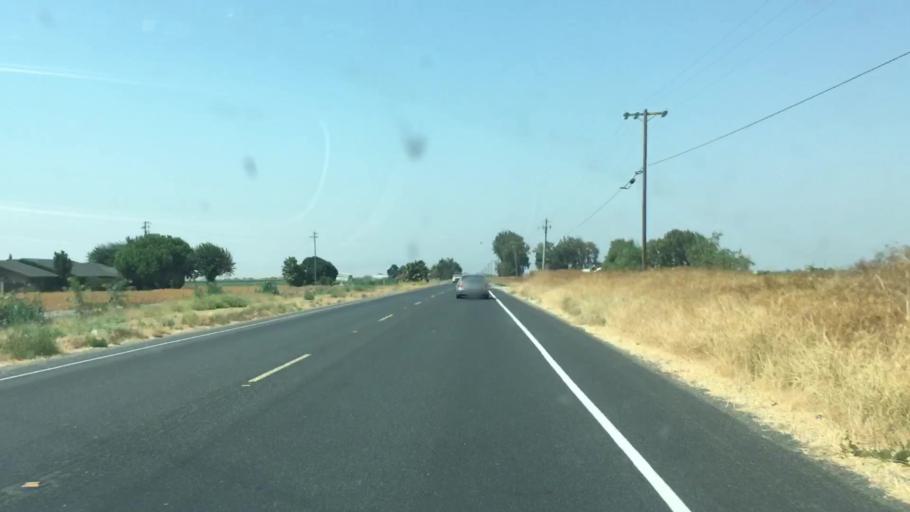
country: US
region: California
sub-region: San Joaquin County
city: Tracy
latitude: 37.8507
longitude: -121.4226
